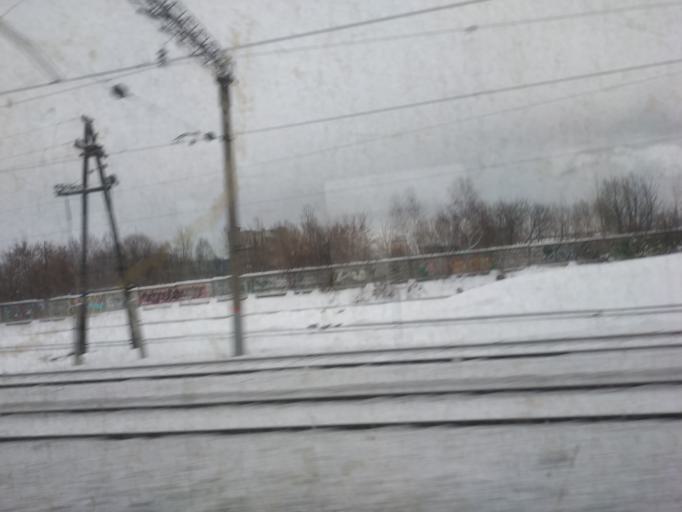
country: RU
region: Moscow
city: Annino
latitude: 55.5843
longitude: 37.6144
